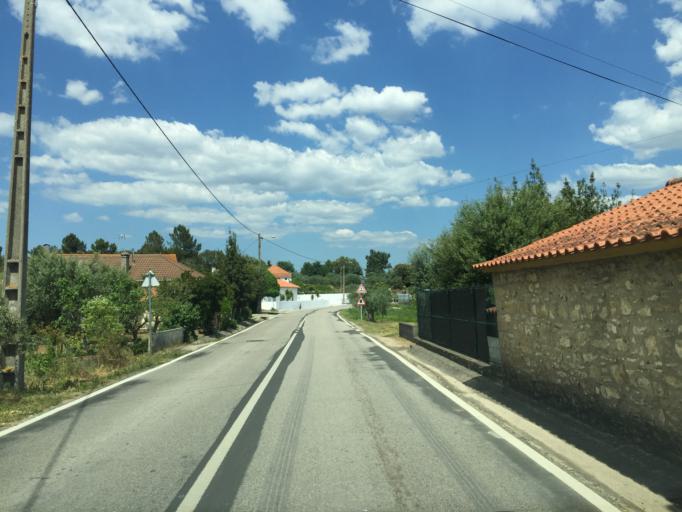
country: PT
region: Santarem
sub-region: Ourem
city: Ourem
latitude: 39.6437
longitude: -8.6136
